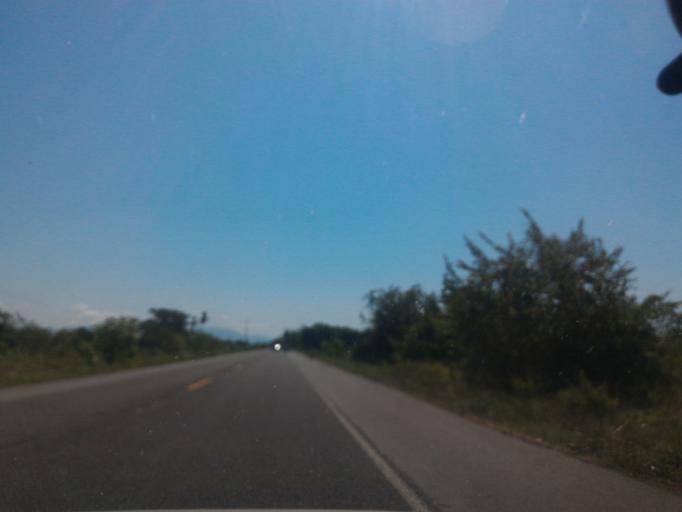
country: MX
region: Michoacan
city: Coahuayana Viejo
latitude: 18.7950
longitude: -103.7932
